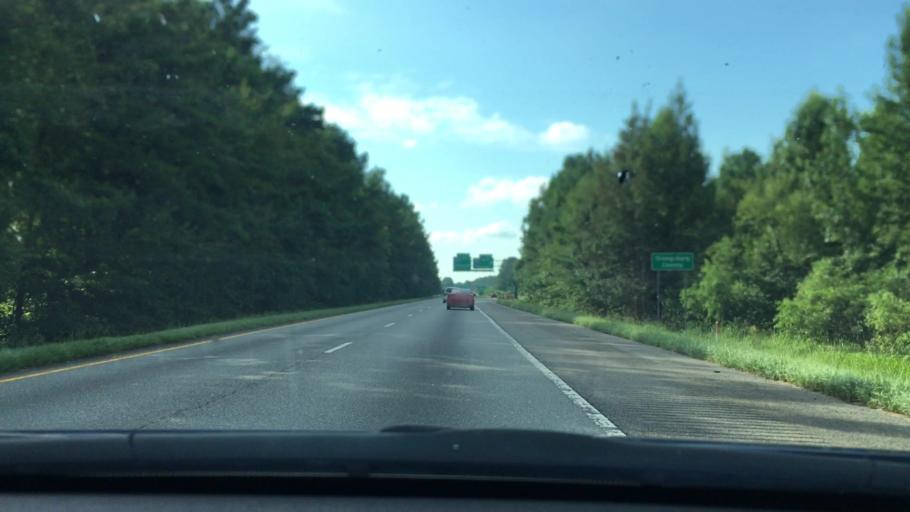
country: US
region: South Carolina
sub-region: Orangeburg County
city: Holly Hill
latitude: 33.3129
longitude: -80.5423
